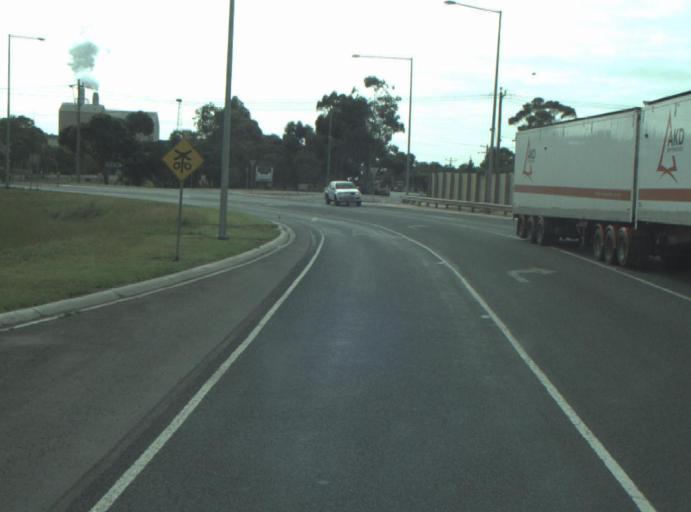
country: AU
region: Victoria
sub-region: Greater Geelong
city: Bell Park
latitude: -38.0949
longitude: 144.3705
